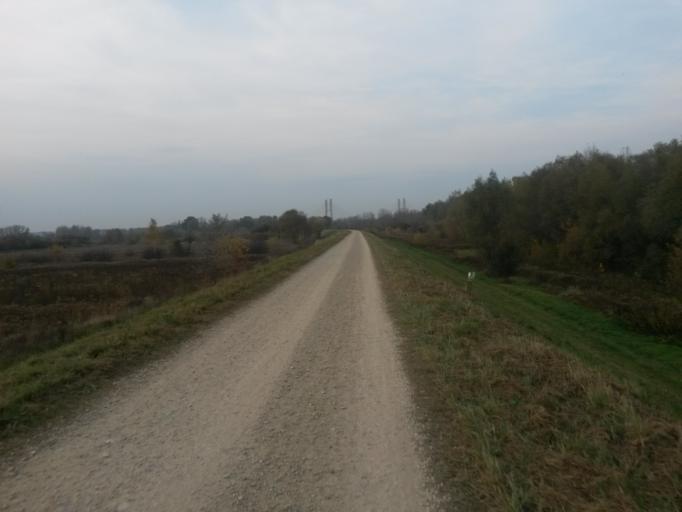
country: PL
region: Masovian Voivodeship
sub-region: Warszawa
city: Wilanow
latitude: 52.2010
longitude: 21.0984
